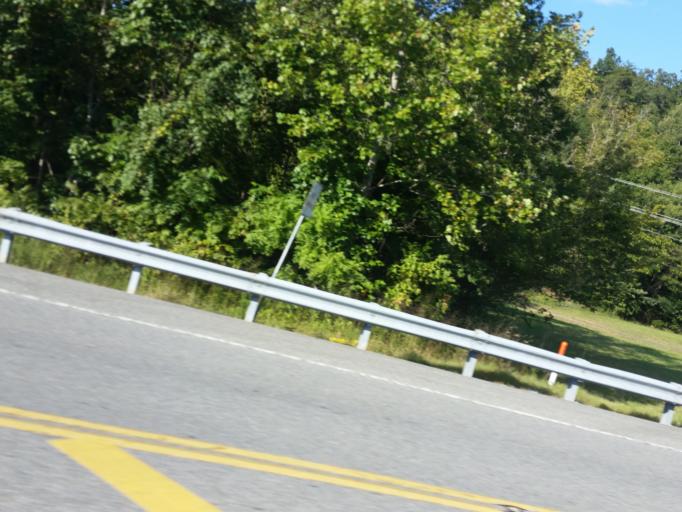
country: US
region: Tennessee
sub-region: Union County
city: Maynardville
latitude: 36.2622
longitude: -83.7790
